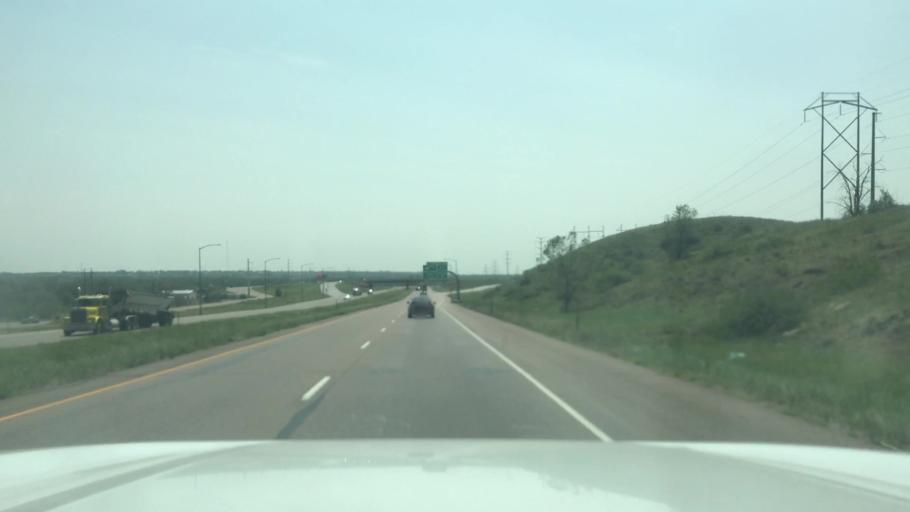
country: US
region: Colorado
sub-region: El Paso County
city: Security-Widefield
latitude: 38.7302
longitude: -104.7387
